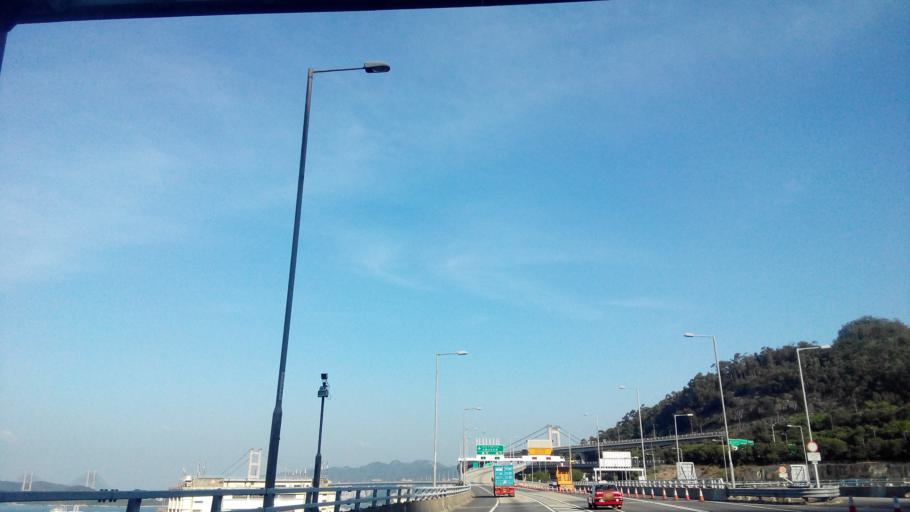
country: HK
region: Tsuen Wan
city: Tsuen Wan
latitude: 22.3420
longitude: 114.0957
